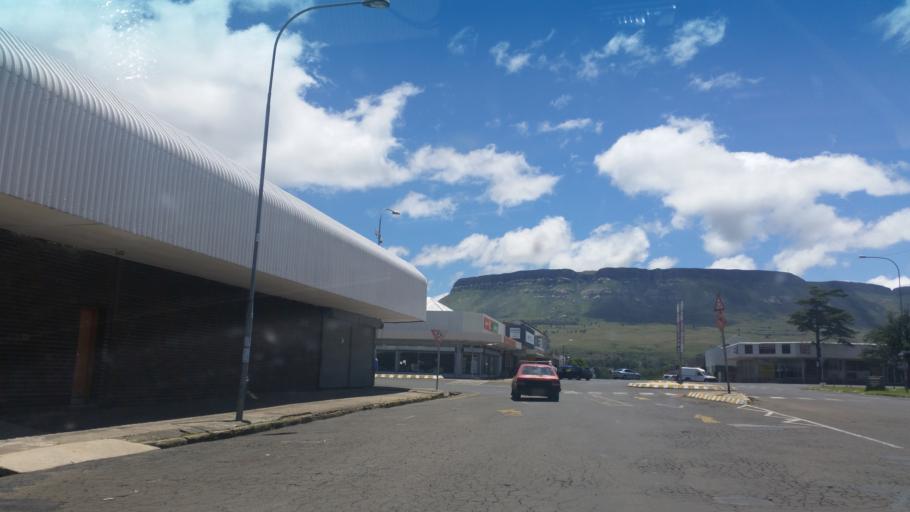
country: ZA
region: Orange Free State
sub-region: Thabo Mofutsanyana District Municipality
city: Harrismith
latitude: -28.2717
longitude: 29.1260
